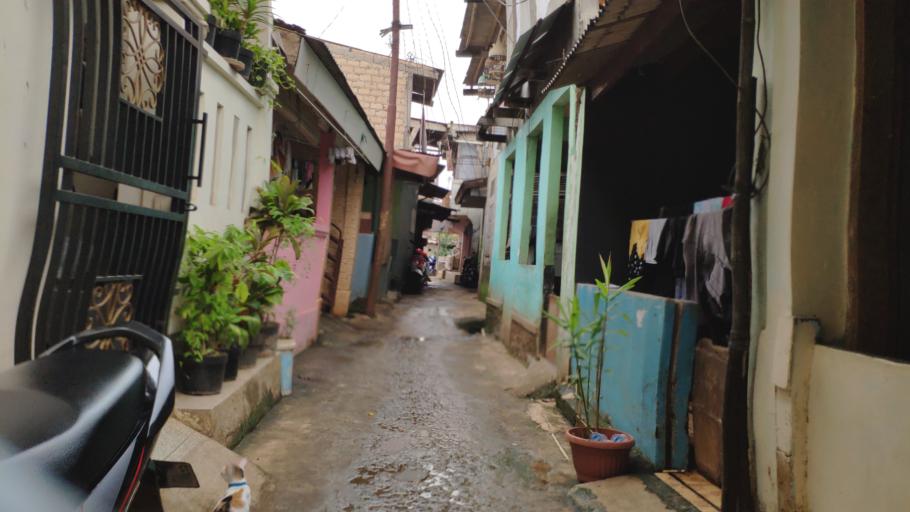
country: ID
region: West Java
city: Pamulang
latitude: -6.2987
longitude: 106.8055
